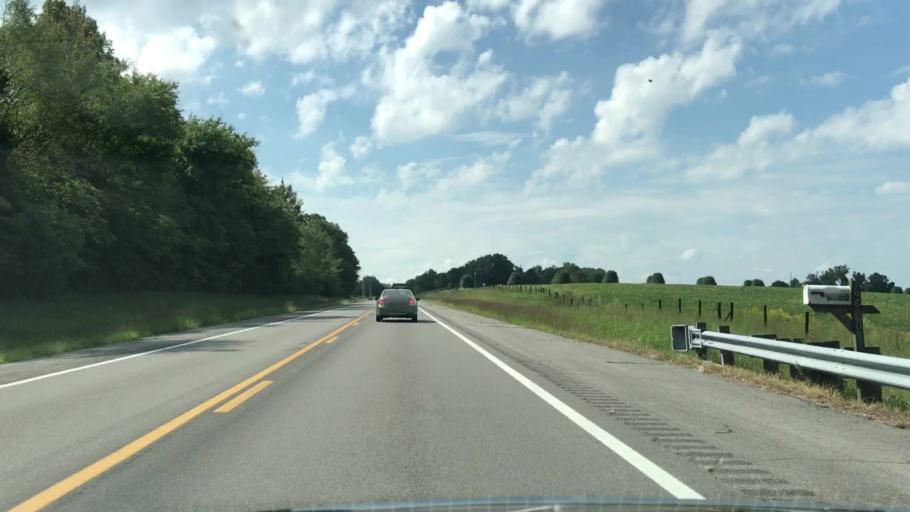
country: US
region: Tennessee
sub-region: Sumner County
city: Westmoreland
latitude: 36.5849
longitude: -86.2390
